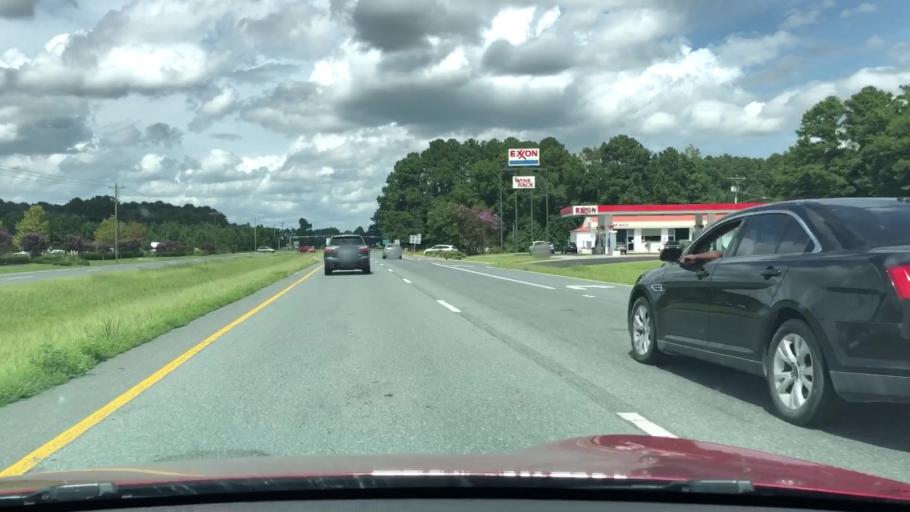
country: US
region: Virginia
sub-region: Accomack County
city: Onancock
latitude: 37.6849
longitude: -75.7224
